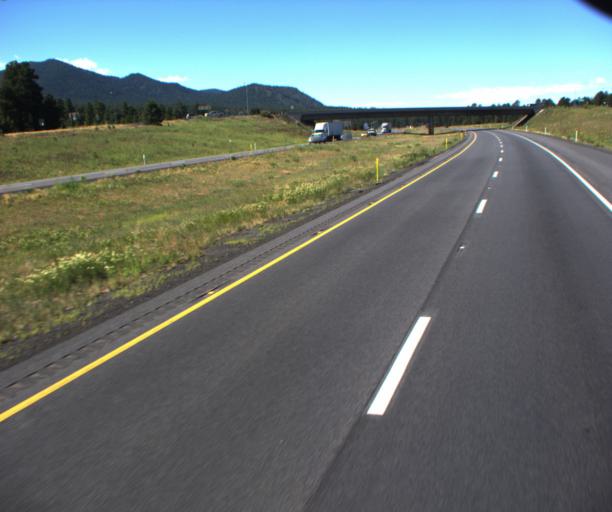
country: US
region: Arizona
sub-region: Coconino County
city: Williams
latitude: 35.2468
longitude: -112.2132
